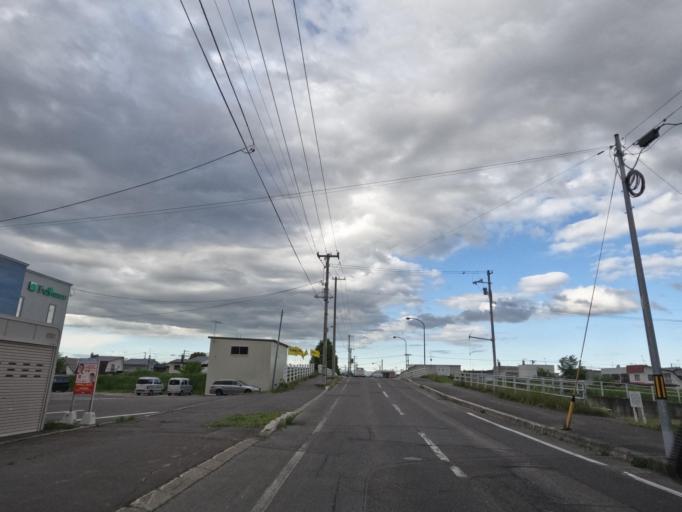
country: JP
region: Hokkaido
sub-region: Asahikawa-shi
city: Asahikawa
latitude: 43.7746
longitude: 142.3141
